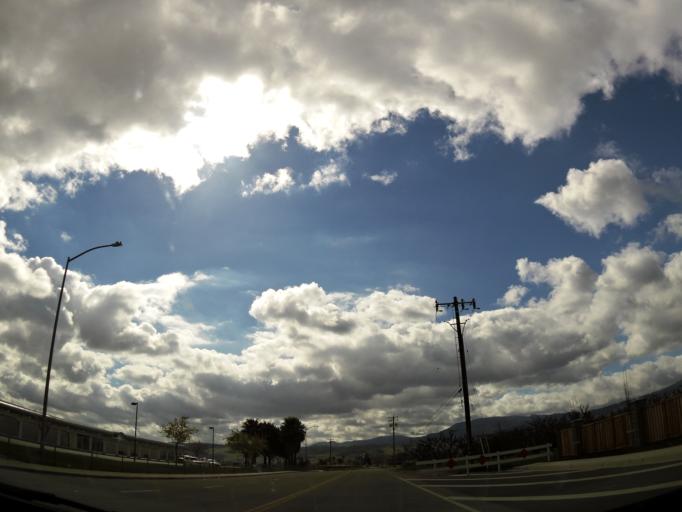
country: US
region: California
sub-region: San Benito County
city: Hollister
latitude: 36.8296
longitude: -121.3932
